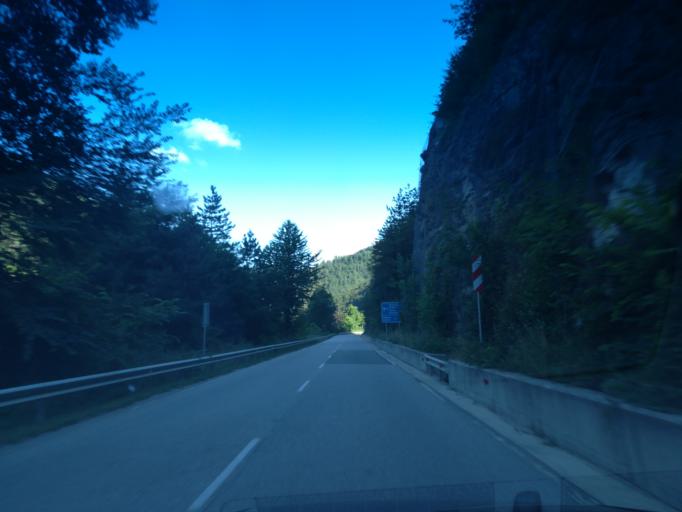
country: BG
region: Smolyan
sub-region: Obshtina Chepelare
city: Chepelare
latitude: 41.8318
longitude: 24.6845
